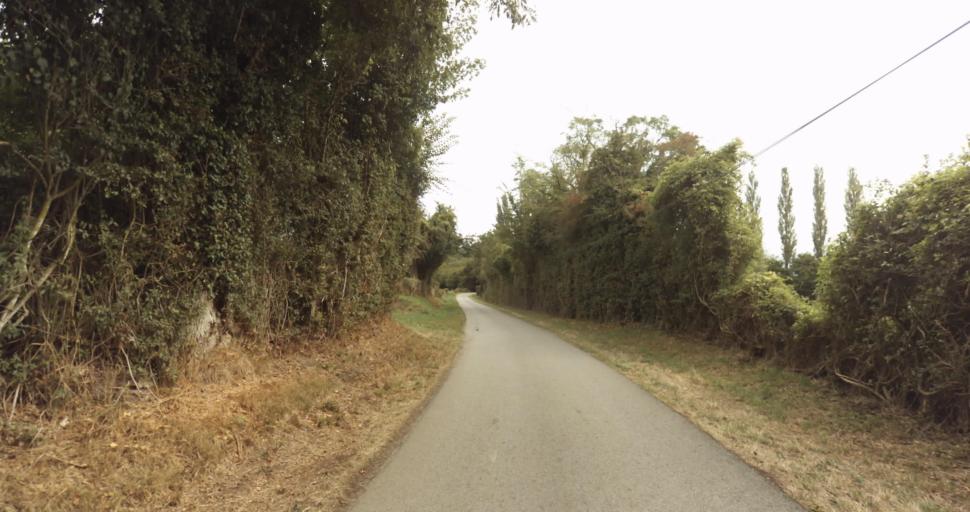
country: FR
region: Lower Normandy
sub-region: Departement de l'Orne
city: Gace
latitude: 48.8287
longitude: 0.2803
